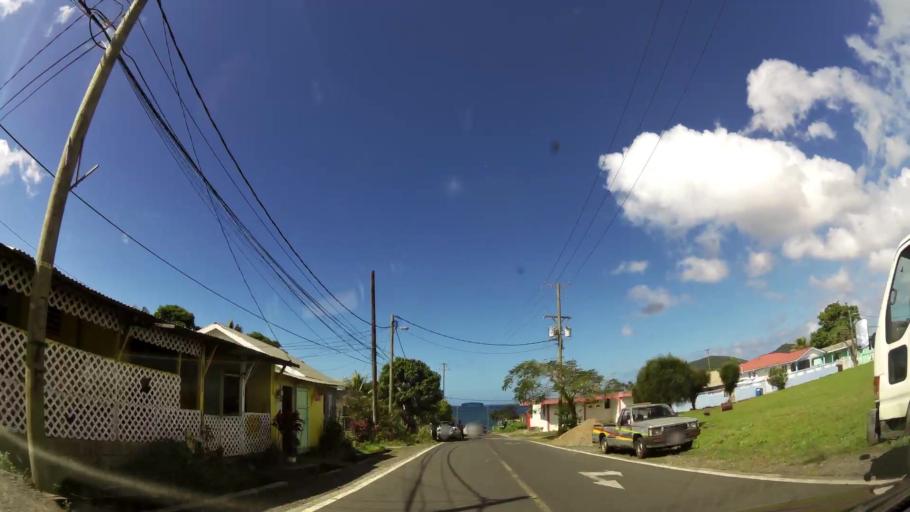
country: DM
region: Saint John
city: Portsmouth
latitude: 15.5653
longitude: -61.4567
